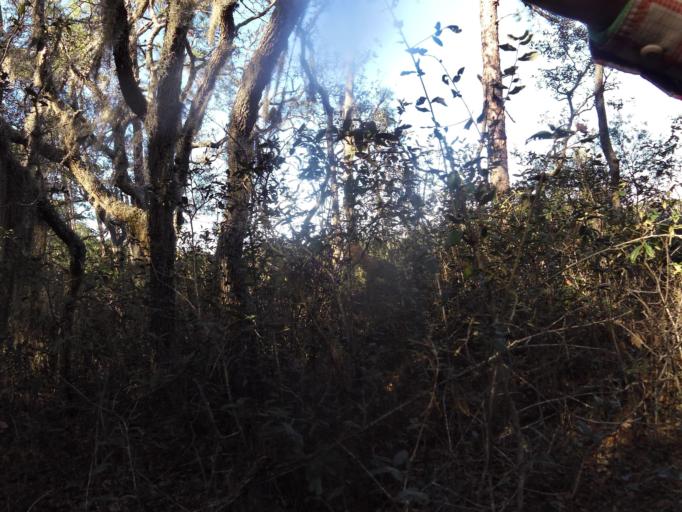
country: US
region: Florida
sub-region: Clay County
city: Keystone Heights
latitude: 29.8223
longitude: -82.0232
